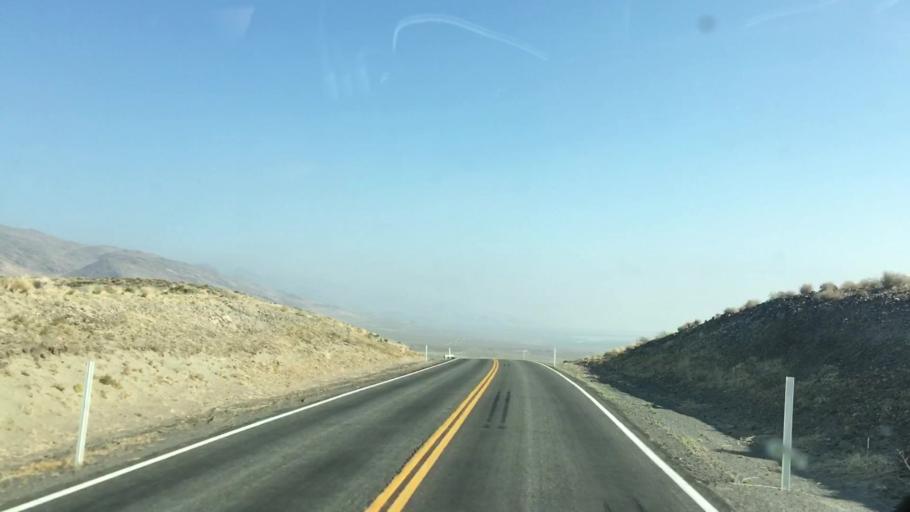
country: US
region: Nevada
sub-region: Lyon County
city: Fernley
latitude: 39.9213
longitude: -119.3810
